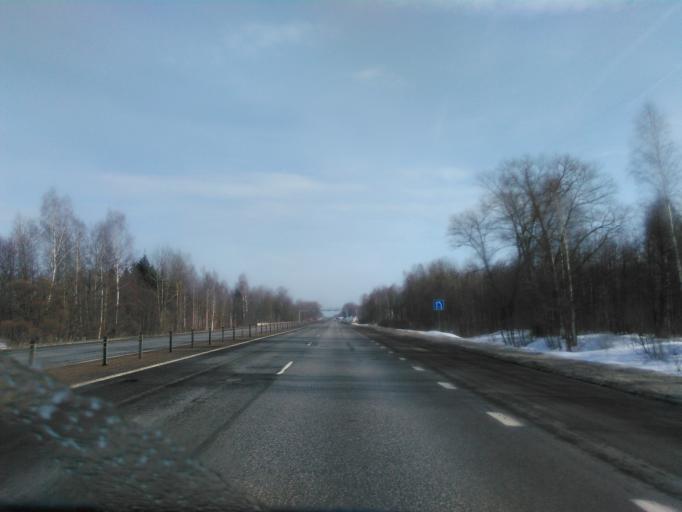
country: BY
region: Vitebsk
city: Dubrowna
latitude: 54.6845
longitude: 30.8043
